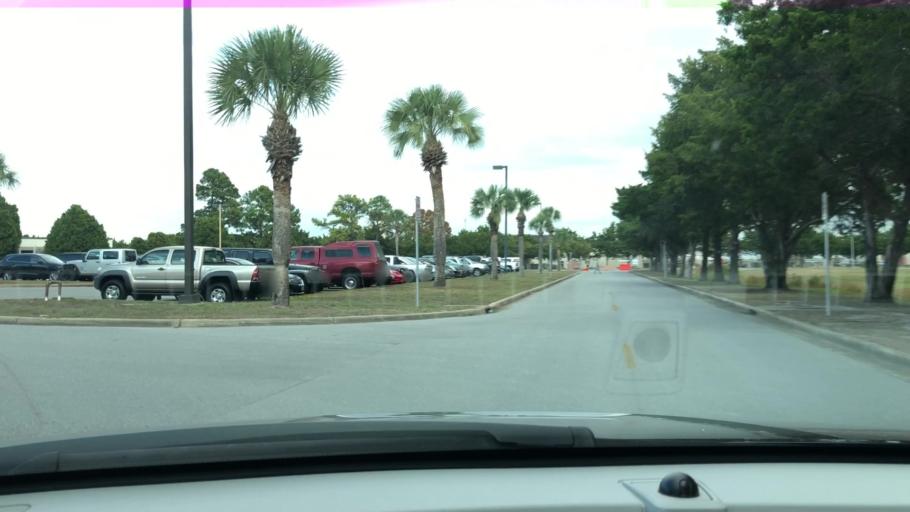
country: US
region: Florida
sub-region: Bay County
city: Tyndall Air Force Base
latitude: 30.0626
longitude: -85.5834
